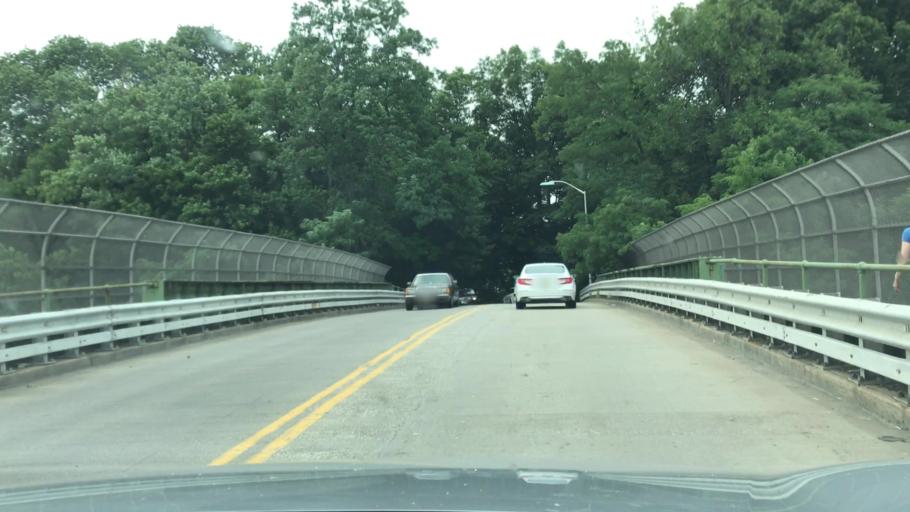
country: US
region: New Jersey
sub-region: Bergen County
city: Teaneck
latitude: 40.9035
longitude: -74.0055
